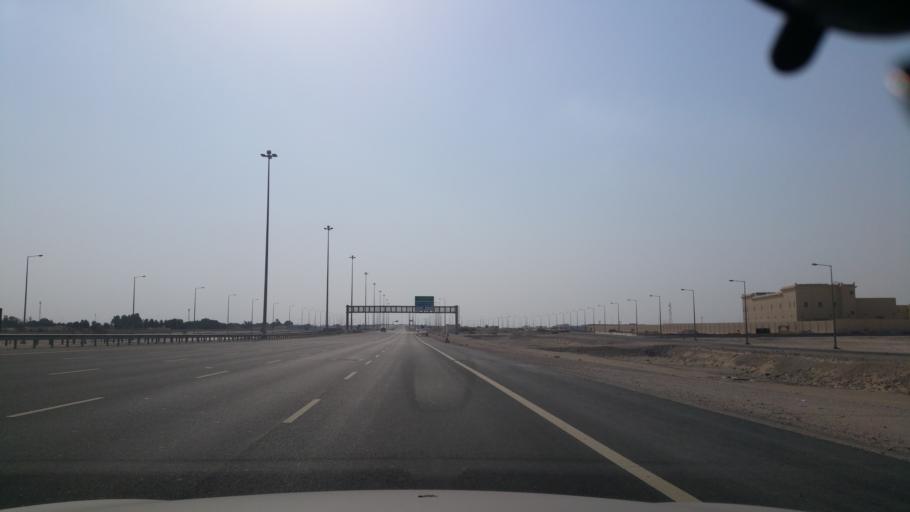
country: QA
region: Baladiyat Umm Salal
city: Umm Salal `Ali
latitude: 25.4524
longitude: 51.4248
